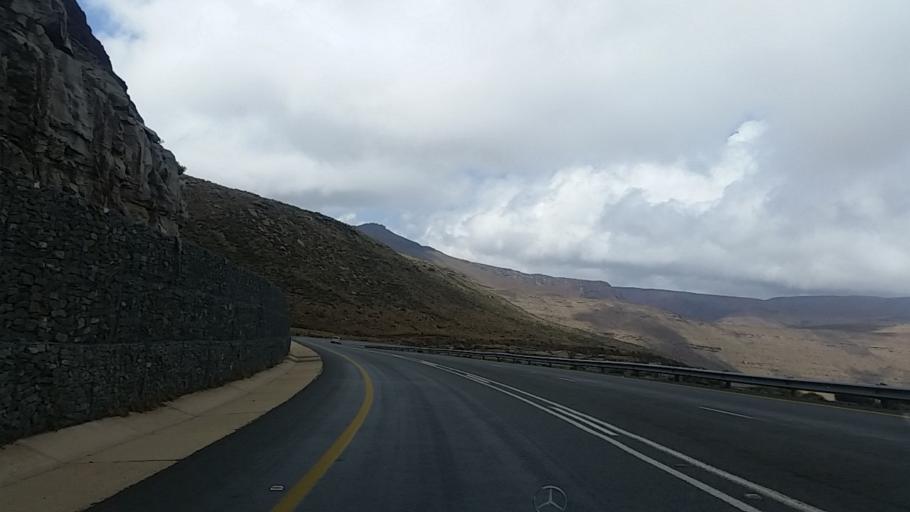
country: ZA
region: Eastern Cape
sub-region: Chris Hani District Municipality
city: Middelburg
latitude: -31.8386
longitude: 24.8633
